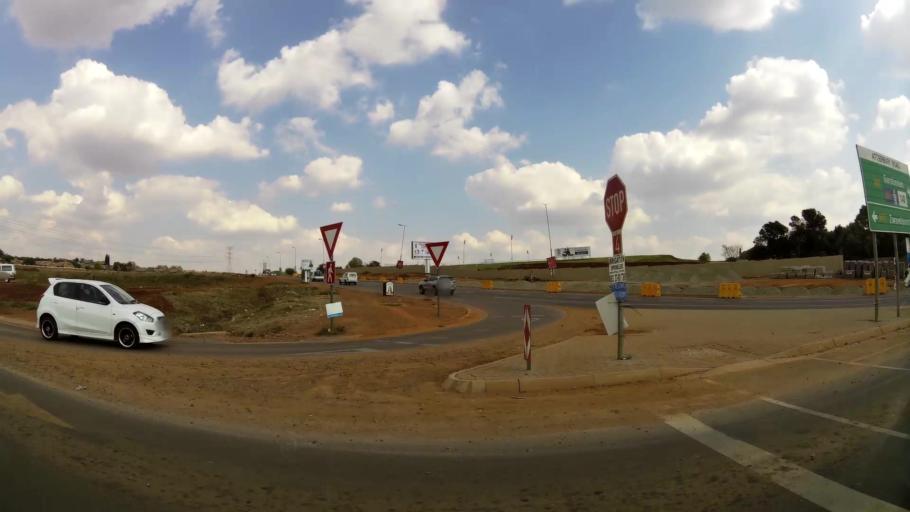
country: ZA
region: Gauteng
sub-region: City of Tshwane Metropolitan Municipality
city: Centurion
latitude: -25.8084
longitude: 28.3291
